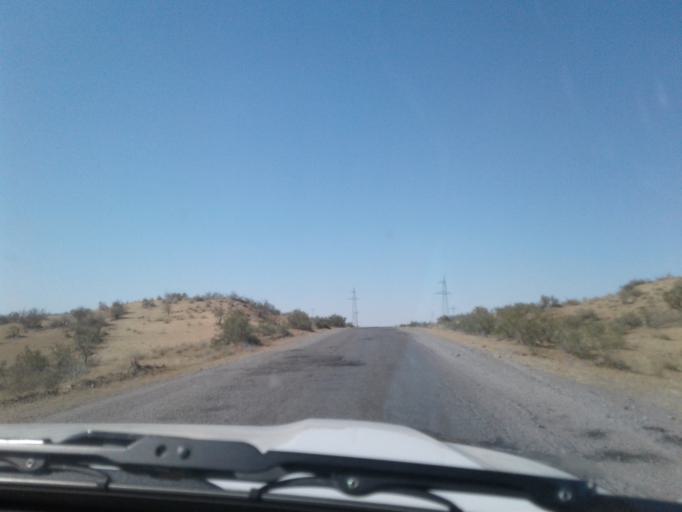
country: AF
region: Badghis
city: Bala Murghab
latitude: 36.2592
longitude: 62.5956
